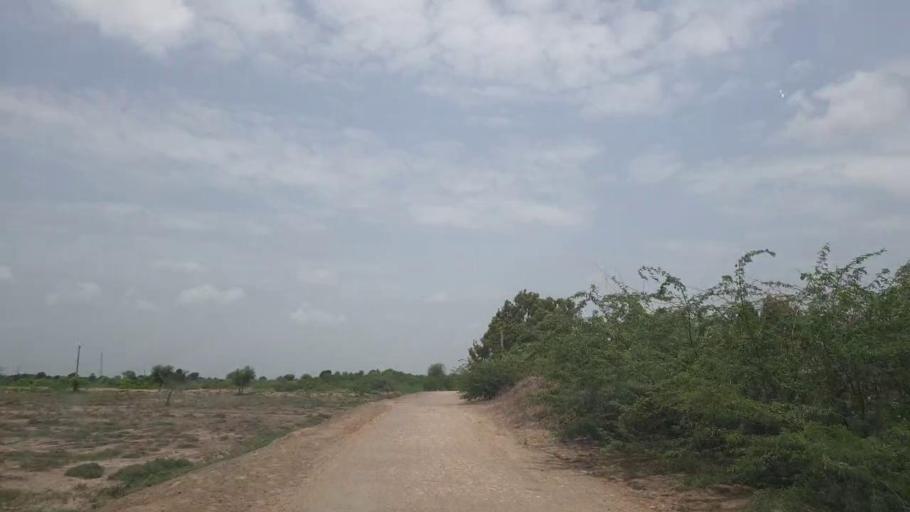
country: PK
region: Sindh
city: Naukot
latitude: 24.9280
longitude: 69.1986
